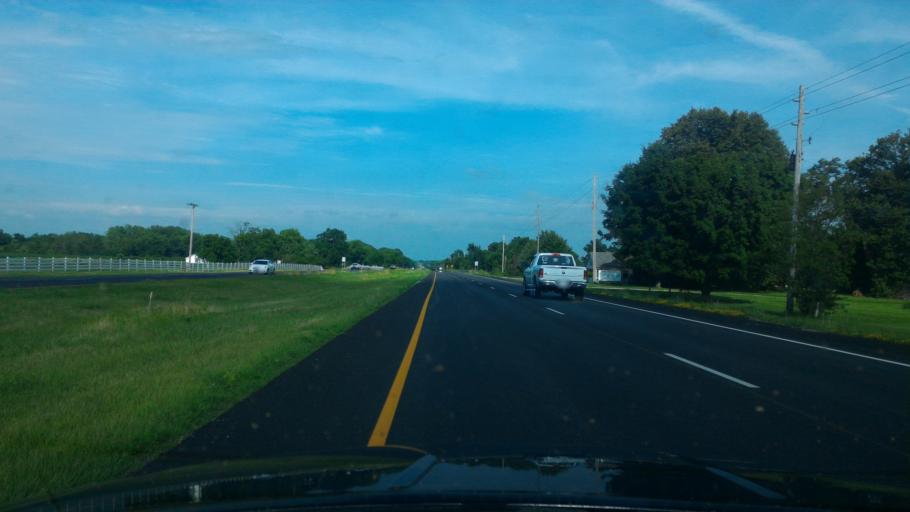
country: US
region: Indiana
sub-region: Tippecanoe County
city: West Lafayette
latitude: 40.4676
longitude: -86.9911
